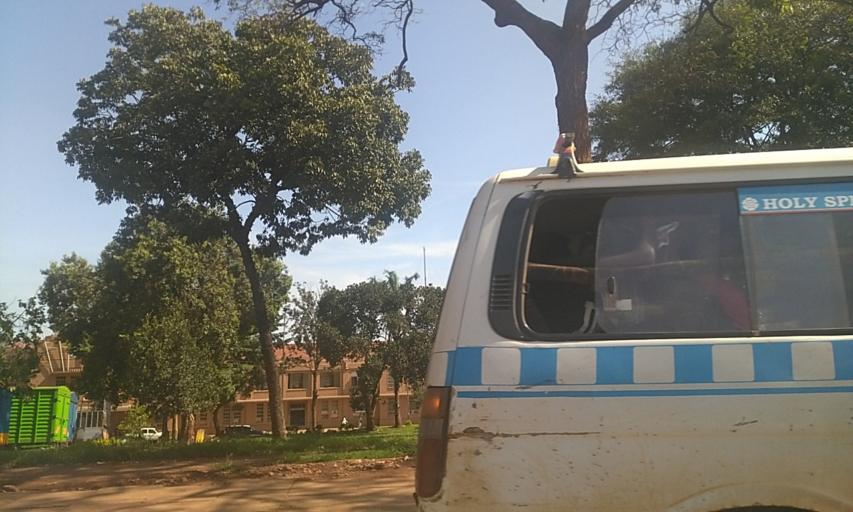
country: UG
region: Central Region
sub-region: Kampala District
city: Kampala
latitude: 0.3131
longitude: 32.5879
